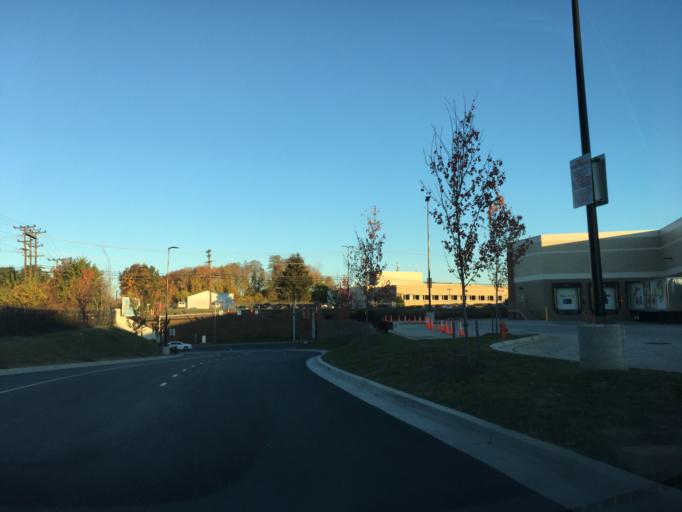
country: US
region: Maryland
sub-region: Baltimore County
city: Owings Mills
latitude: 39.4126
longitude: -76.7755
